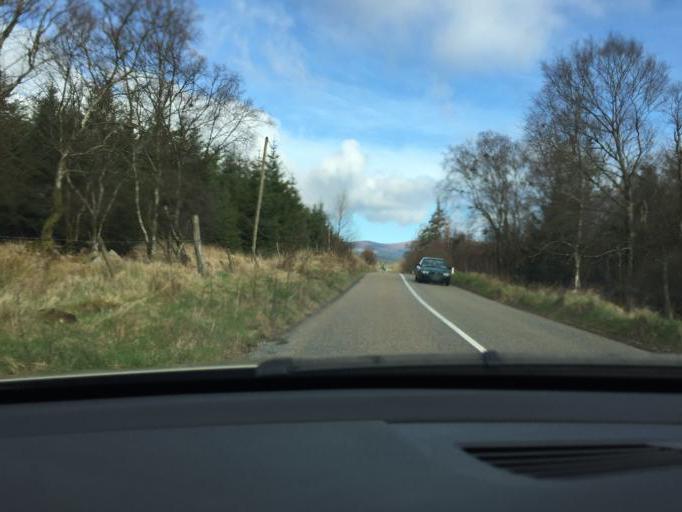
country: IE
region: Leinster
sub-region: Wicklow
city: Valleymount
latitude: 53.0605
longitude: -6.4975
